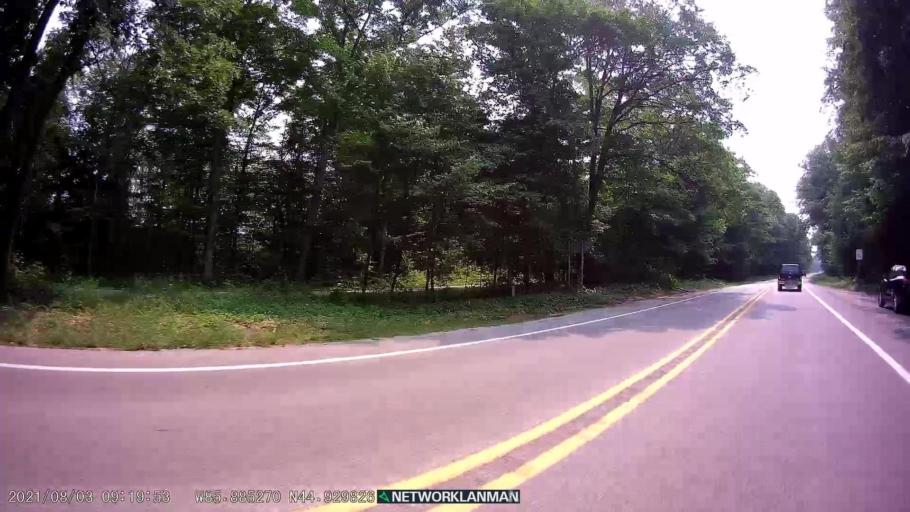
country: US
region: Michigan
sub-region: Leelanau County
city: Leland
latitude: 44.9296
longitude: -85.8850
